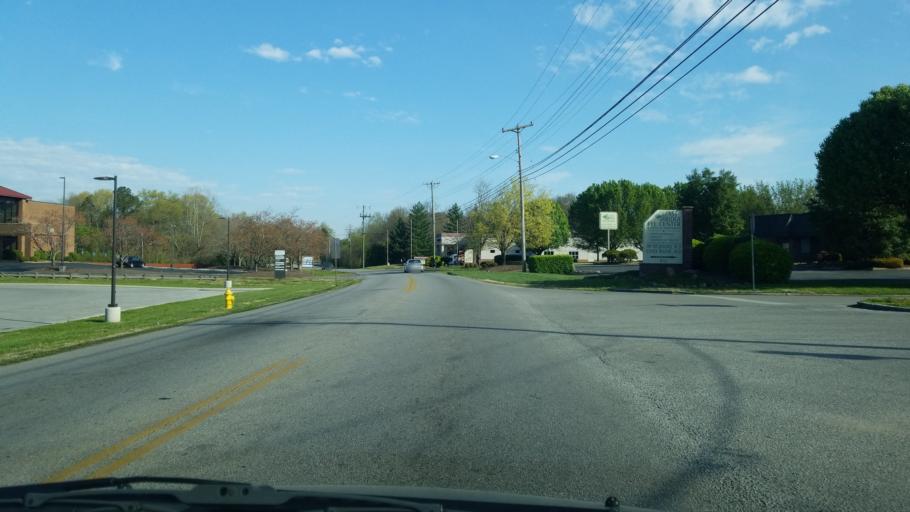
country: US
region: Tennessee
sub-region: Hamilton County
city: East Ridge
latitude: 34.9990
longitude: -85.2178
